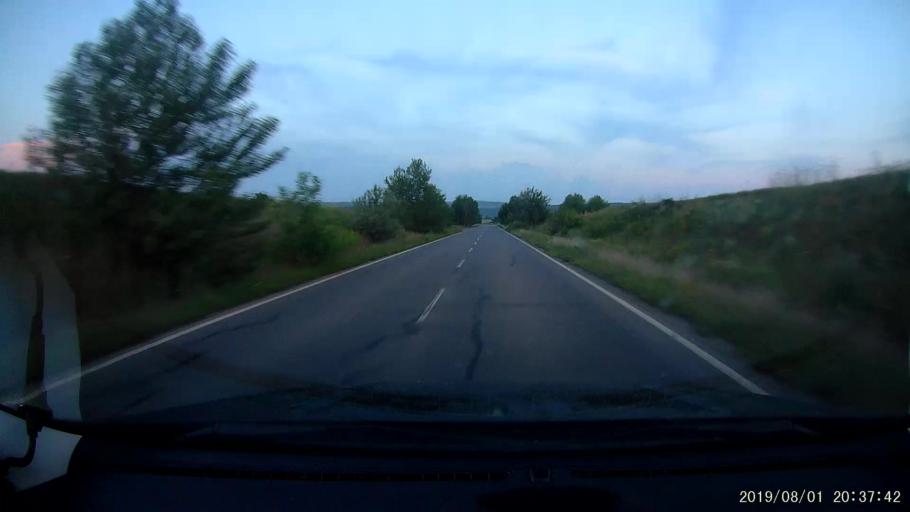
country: BG
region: Yambol
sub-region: Obshtina Elkhovo
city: Elkhovo
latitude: 42.0423
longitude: 26.5954
